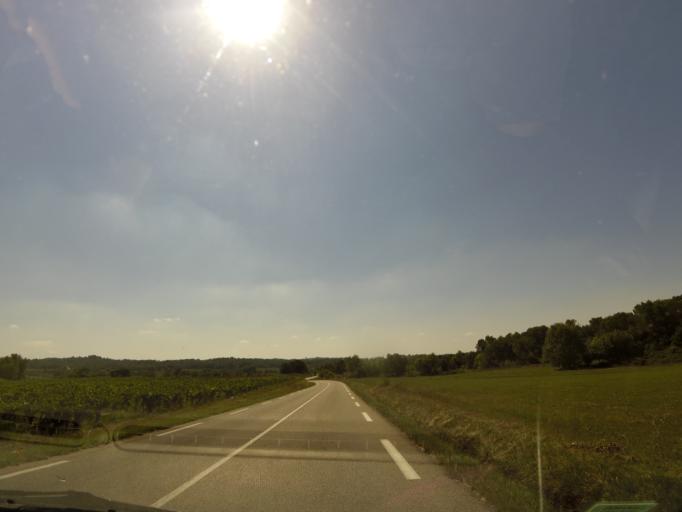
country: FR
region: Languedoc-Roussillon
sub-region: Departement du Gard
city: Villevieille
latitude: 43.8208
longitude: 4.0955
